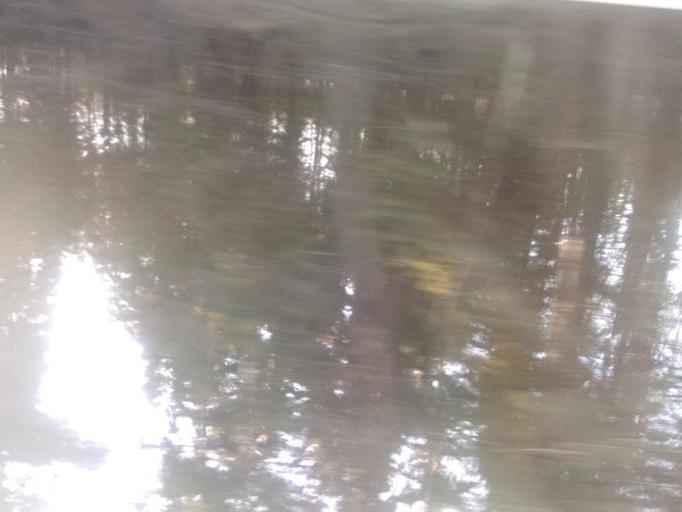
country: RU
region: Moskovskaya
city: Zhavoronki
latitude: 55.6043
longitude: 37.1059
